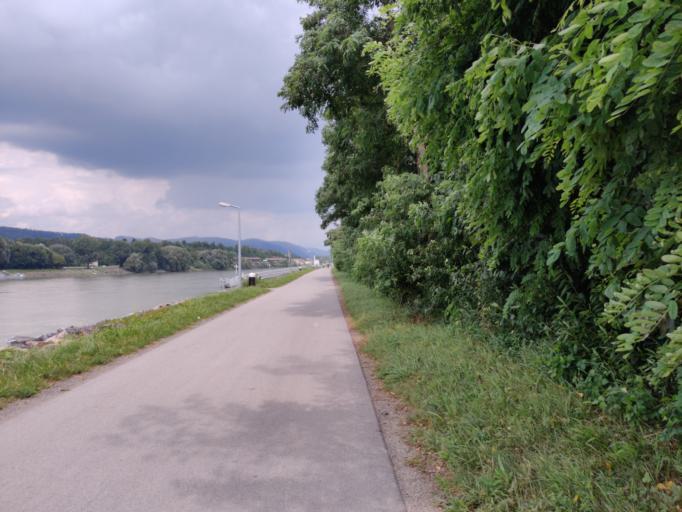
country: AT
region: Lower Austria
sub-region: Politischer Bezirk Melk
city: Melk
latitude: 48.2314
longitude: 15.3243
